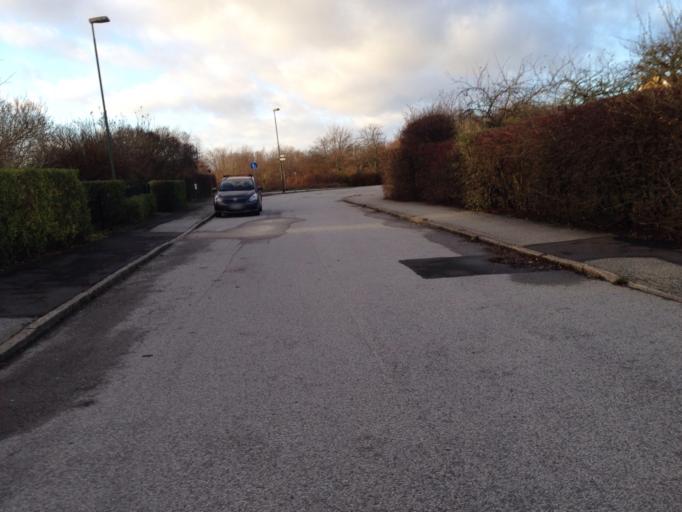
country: SE
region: Skane
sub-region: Lunds Kommun
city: Lund
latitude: 55.7180
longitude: 13.1798
